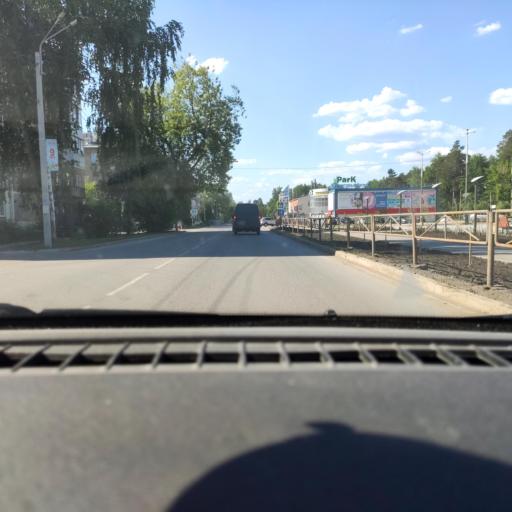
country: RU
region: Perm
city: Krasnokamsk
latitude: 58.0815
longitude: 55.7579
